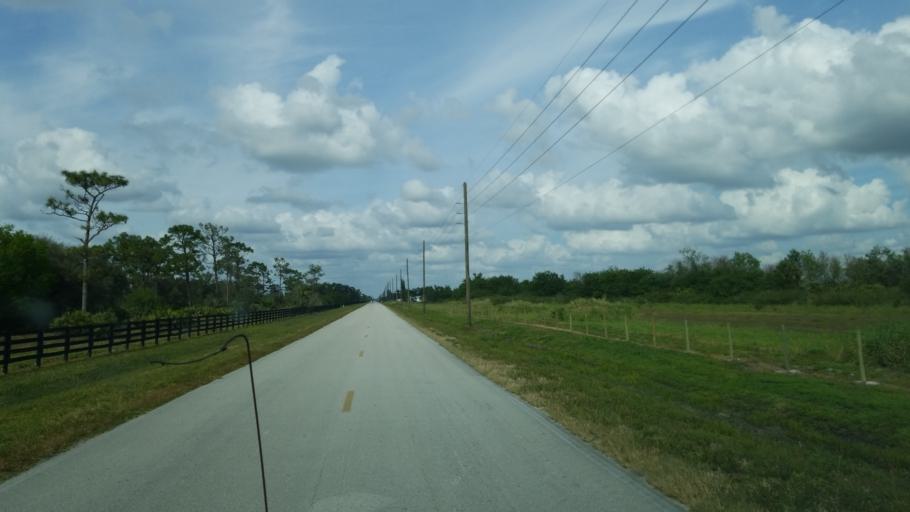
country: US
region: Florida
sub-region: Okeechobee County
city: Cypress Quarters
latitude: 27.4755
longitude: -80.7715
